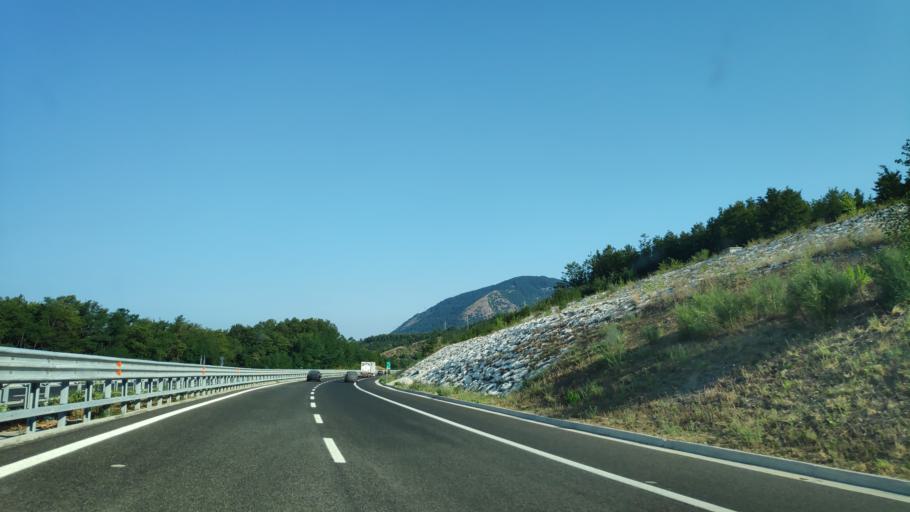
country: IT
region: Basilicate
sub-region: Provincia di Potenza
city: Nemoli
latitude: 40.1034
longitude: 15.7971
